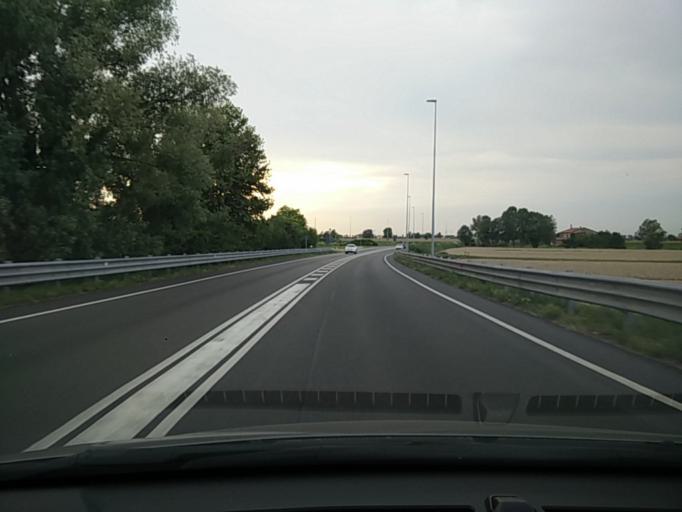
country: IT
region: Veneto
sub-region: Provincia di Venezia
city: Iesolo
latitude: 45.5406
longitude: 12.6227
